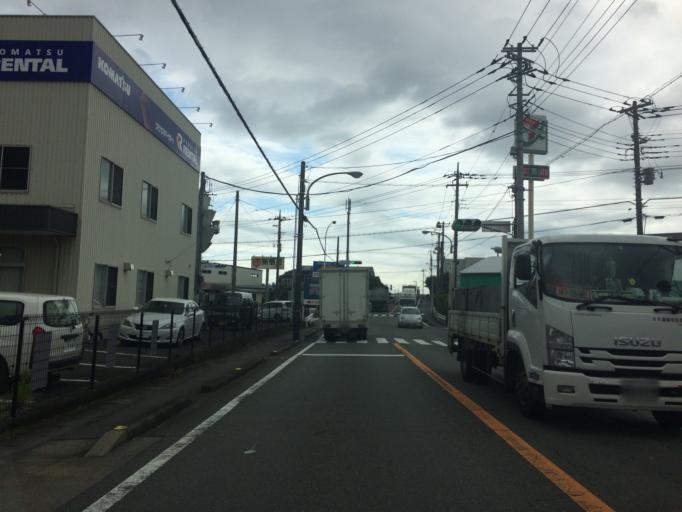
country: JP
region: Shizuoka
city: Fuji
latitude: 35.1788
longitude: 138.6477
